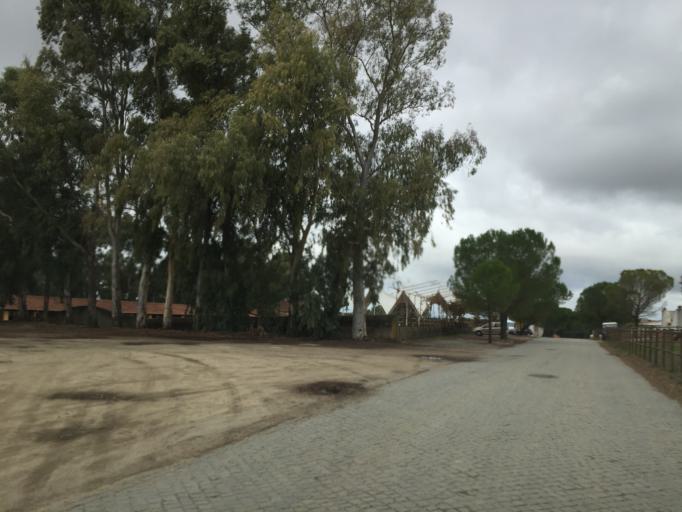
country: PT
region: Portalegre
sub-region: Alter do Chao
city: Alter do Chao
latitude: 39.2210
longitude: -7.6855
